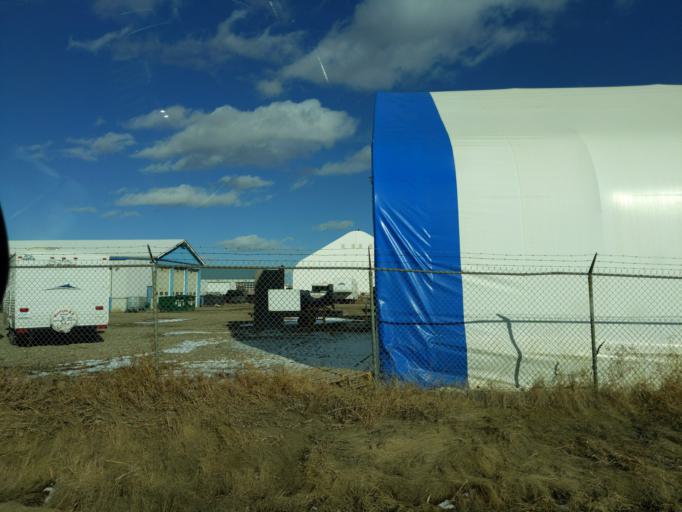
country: CA
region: Saskatchewan
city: Lloydminster
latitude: 53.2768
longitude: -109.9703
